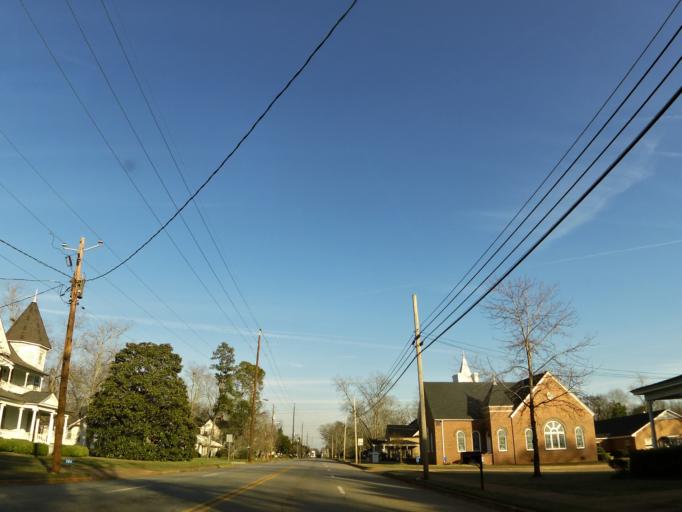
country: US
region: Georgia
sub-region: Webster County
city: Preston
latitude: 32.0340
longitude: -84.3986
